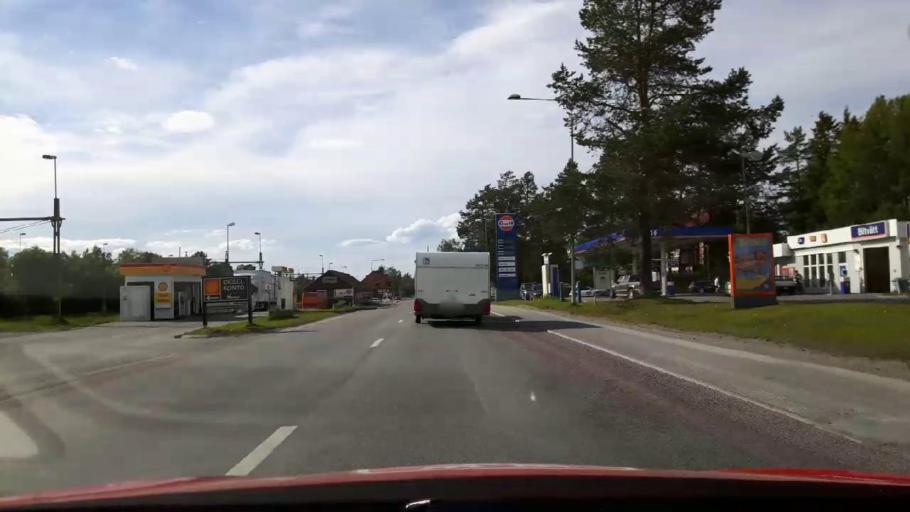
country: SE
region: Jaemtland
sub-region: OEstersunds Kommun
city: Brunflo
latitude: 63.0810
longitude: 14.8244
